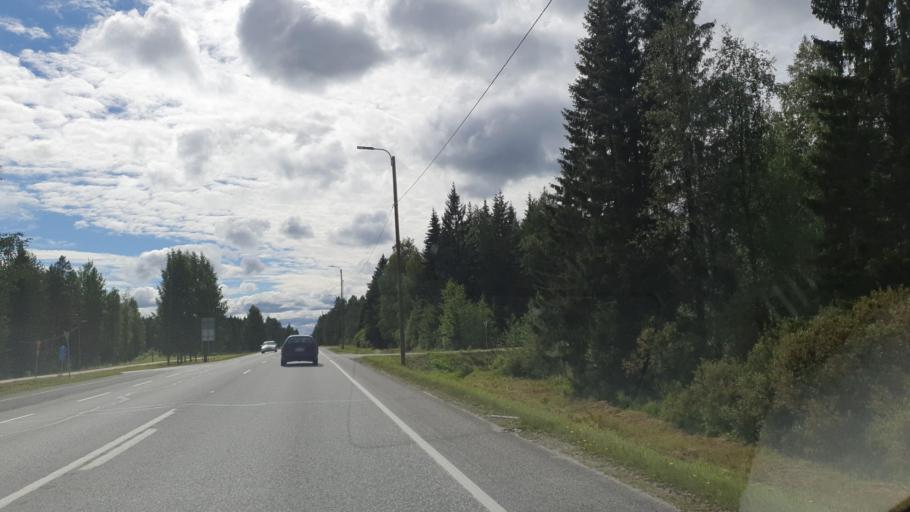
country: FI
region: Kainuu
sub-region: Kajaani
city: Kajaani
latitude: 64.2073
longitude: 27.6510
